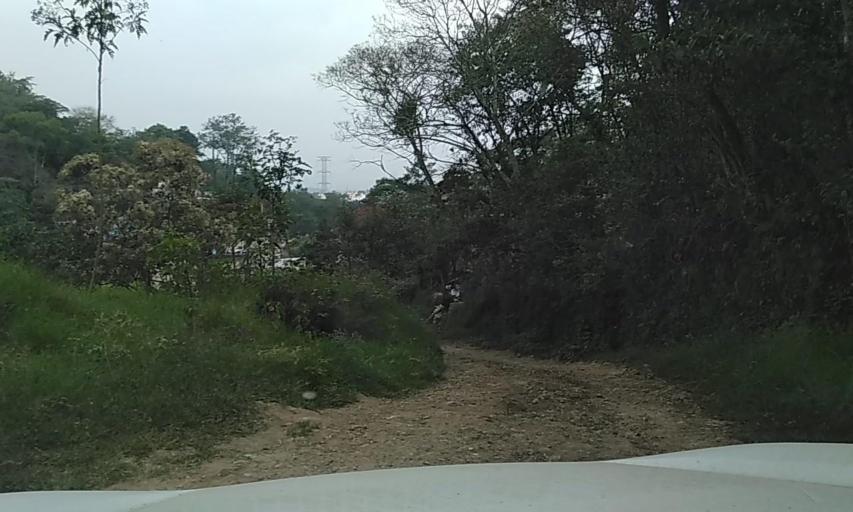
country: MX
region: Veracruz
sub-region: Xalapa
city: Lomas Verdes
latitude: 19.5003
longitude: -96.9188
